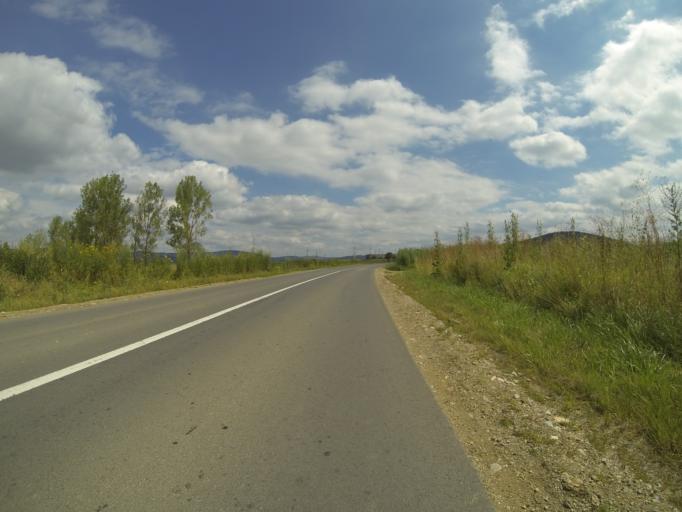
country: RO
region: Brasov
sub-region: Comuna Hoghiz
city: Hoghiz
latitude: 45.9786
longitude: 25.3183
